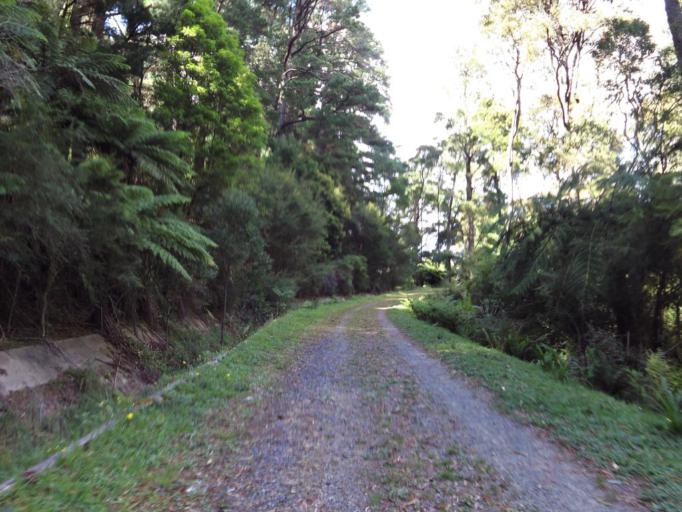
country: AU
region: Victoria
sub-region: Yarra Ranges
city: Millgrove
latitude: -37.7444
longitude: 145.6810
